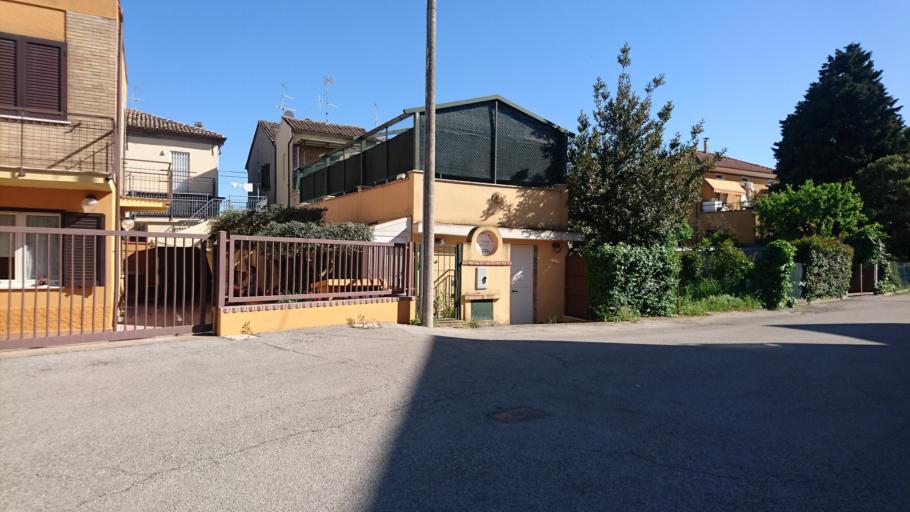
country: IT
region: The Marches
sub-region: Provincia di Pesaro e Urbino
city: Pesaro
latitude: 43.8974
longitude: 12.8952
